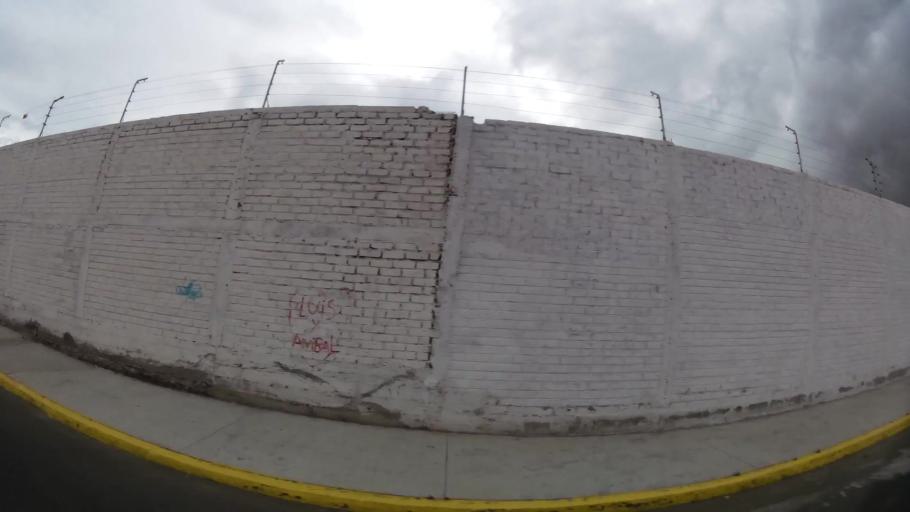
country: EC
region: Tungurahua
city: Ambato
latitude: -1.2633
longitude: -78.6152
